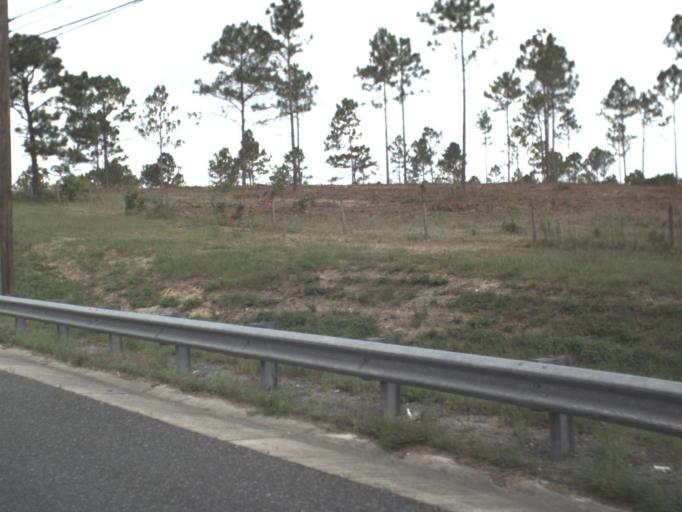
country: US
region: Florida
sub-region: Hernando County
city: Hill 'n Dale
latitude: 28.5233
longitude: -82.2731
